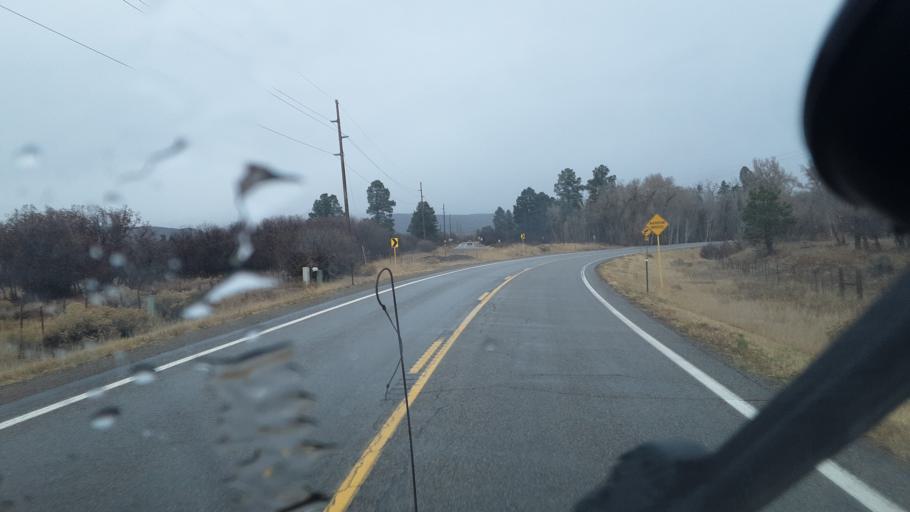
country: US
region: Colorado
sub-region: La Plata County
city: Durango
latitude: 37.2486
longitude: -108.0363
